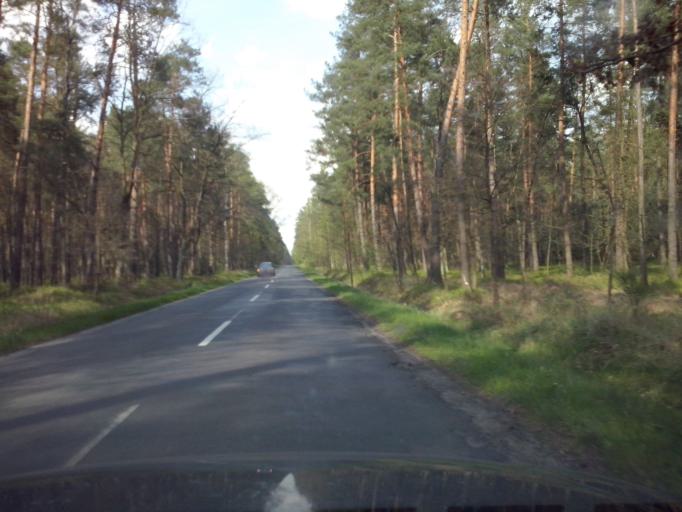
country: PL
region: Subcarpathian Voivodeship
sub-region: Powiat lezajski
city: Letownia
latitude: 50.3772
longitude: 22.2557
